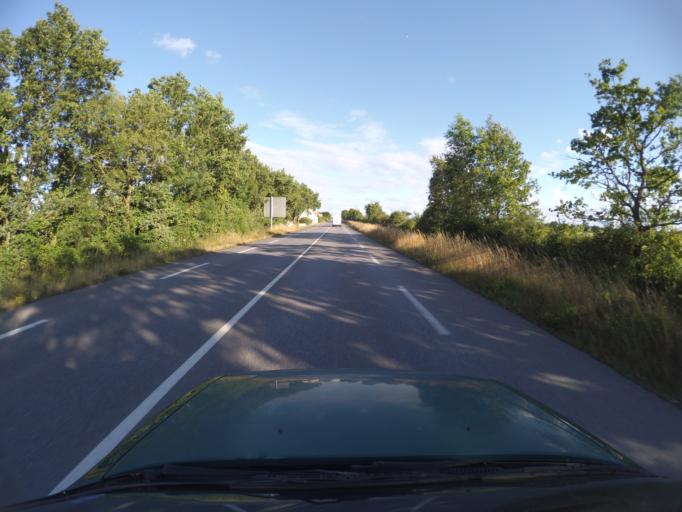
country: FR
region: Pays de la Loire
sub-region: Departement de la Vendee
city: Saint-Hilaire-de-Loulay
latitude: 47.0159
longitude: -1.3421
